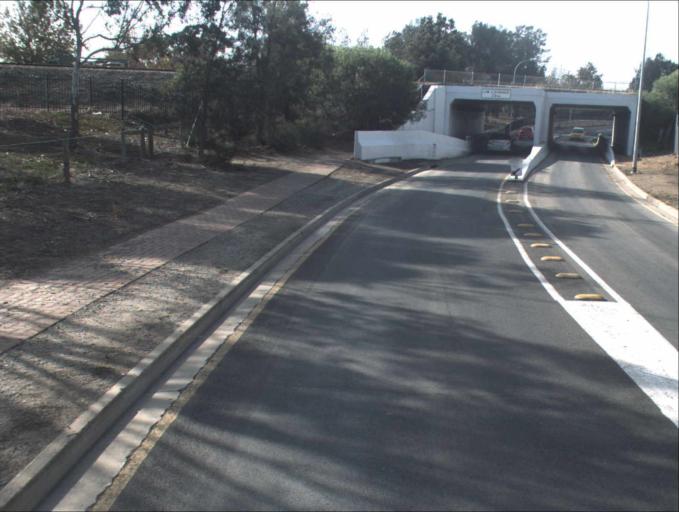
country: AU
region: South Australia
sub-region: Port Adelaide Enfield
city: Birkenhead
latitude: -34.8506
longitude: 138.5019
